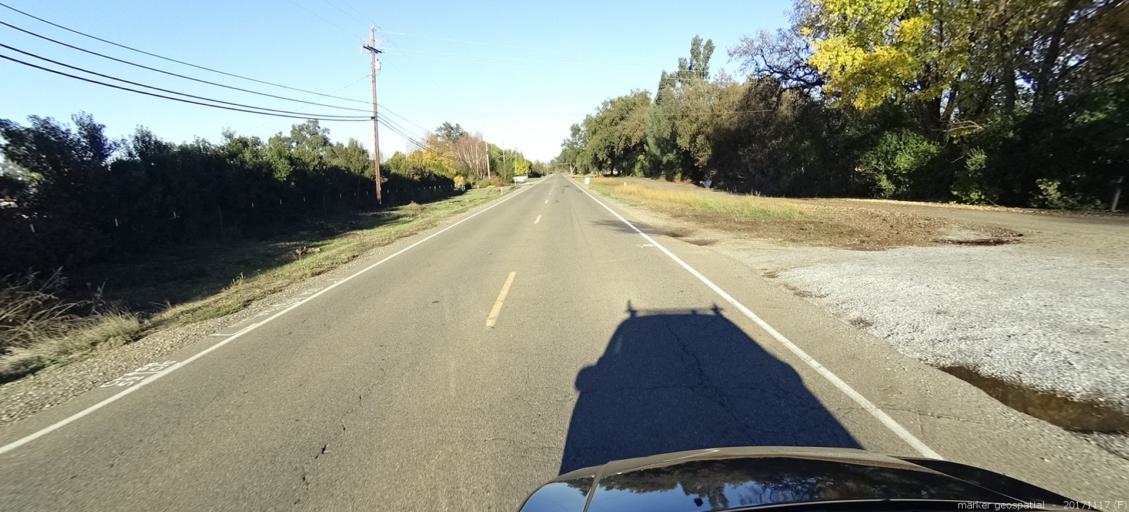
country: US
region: California
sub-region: Shasta County
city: Anderson
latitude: 40.4504
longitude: -122.2544
